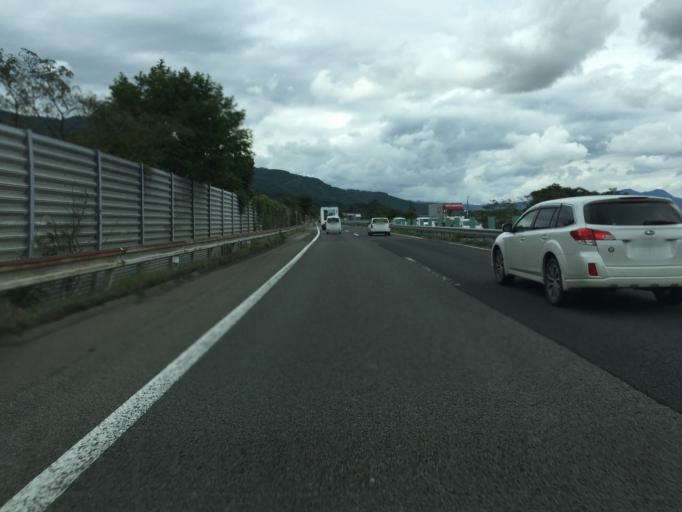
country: JP
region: Miyagi
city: Shiroishi
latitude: 37.9647
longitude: 140.6184
